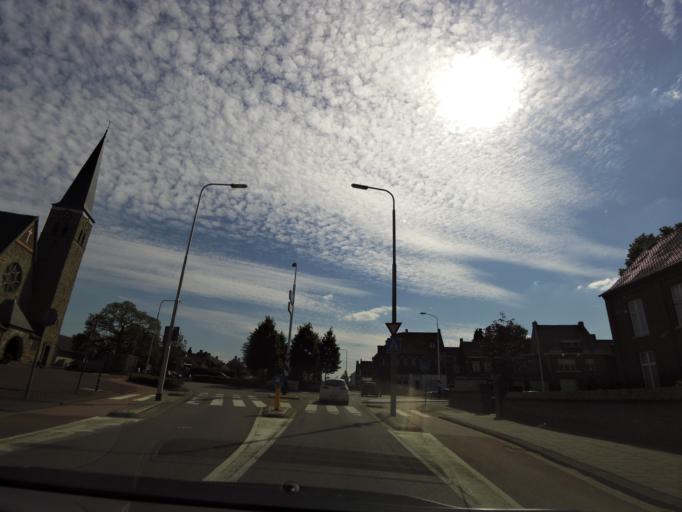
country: NL
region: Limburg
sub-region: Gemeente Echt-Susteren
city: Koningsbosch
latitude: 51.0518
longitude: 5.9585
